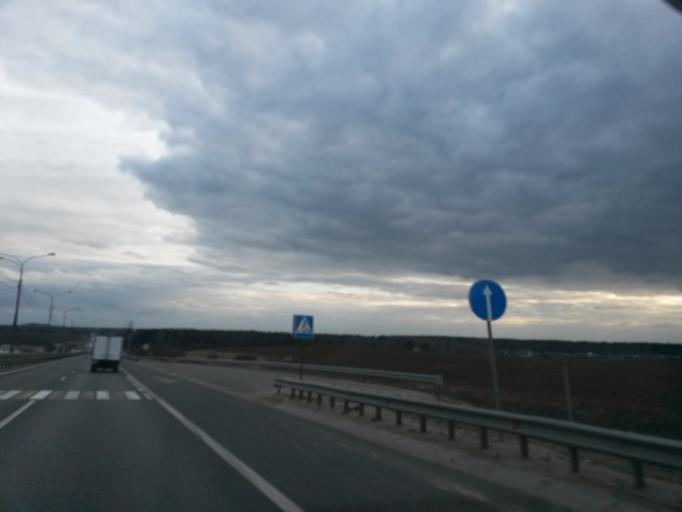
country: RU
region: Moskovskaya
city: Svatkovo
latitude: 56.3354
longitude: 38.2593
